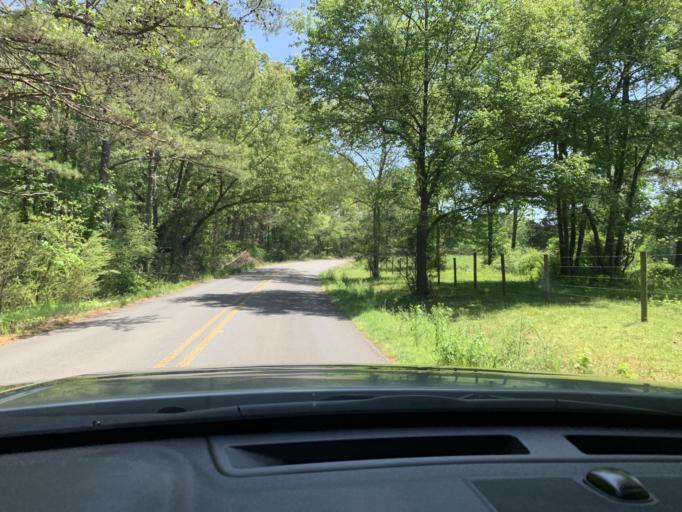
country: US
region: Georgia
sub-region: Polk County
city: Aragon
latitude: 34.0894
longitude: -85.1284
